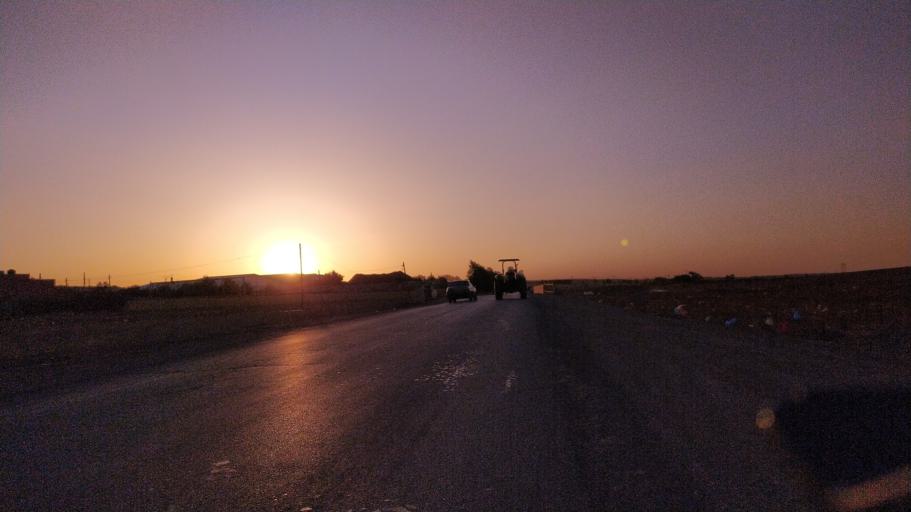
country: DZ
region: Tiaret
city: Frenda
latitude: 34.9022
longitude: 1.2406
